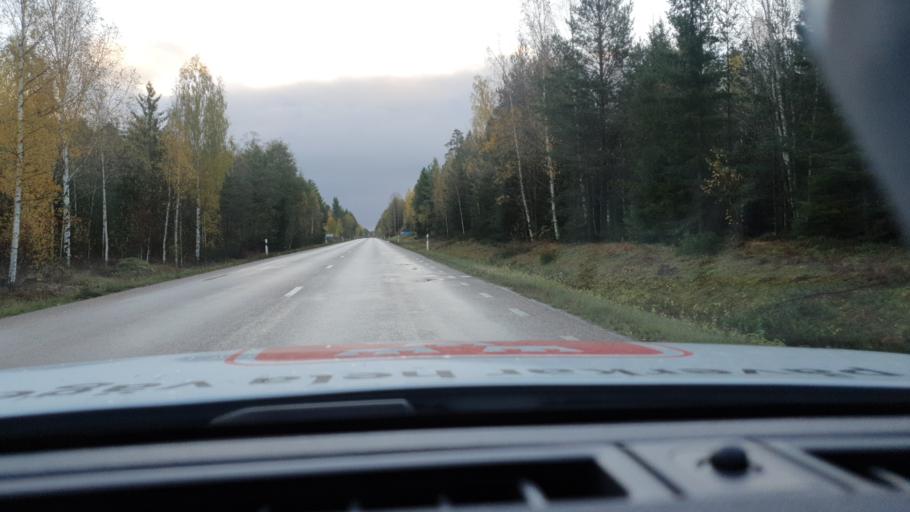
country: SE
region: Uppsala
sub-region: Tierps Kommun
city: Orbyhus
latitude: 60.2143
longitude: 17.7540
